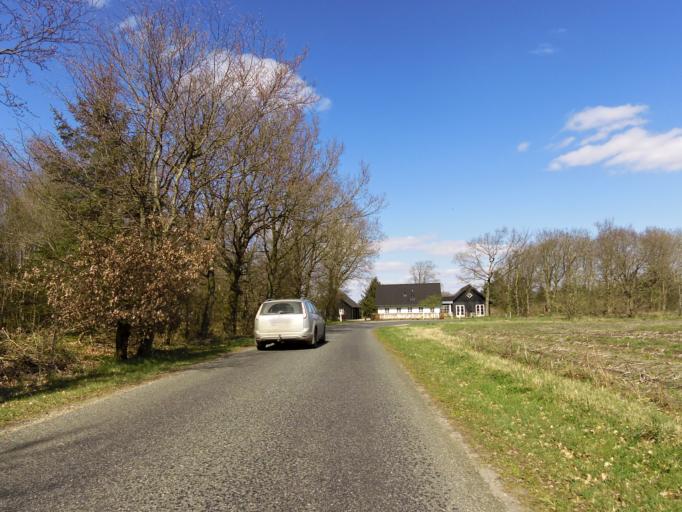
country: DK
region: South Denmark
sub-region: Esbjerg Kommune
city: Ribe
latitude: 55.3447
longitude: 8.8313
